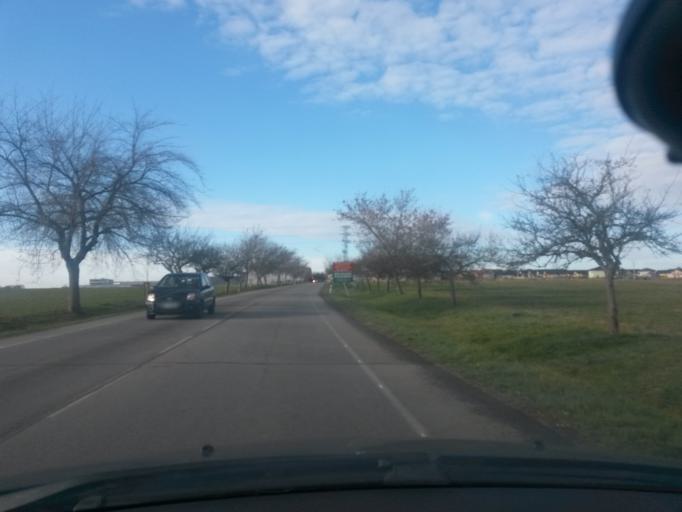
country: CZ
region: Central Bohemia
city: Jesenice
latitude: 49.9701
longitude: 14.5361
